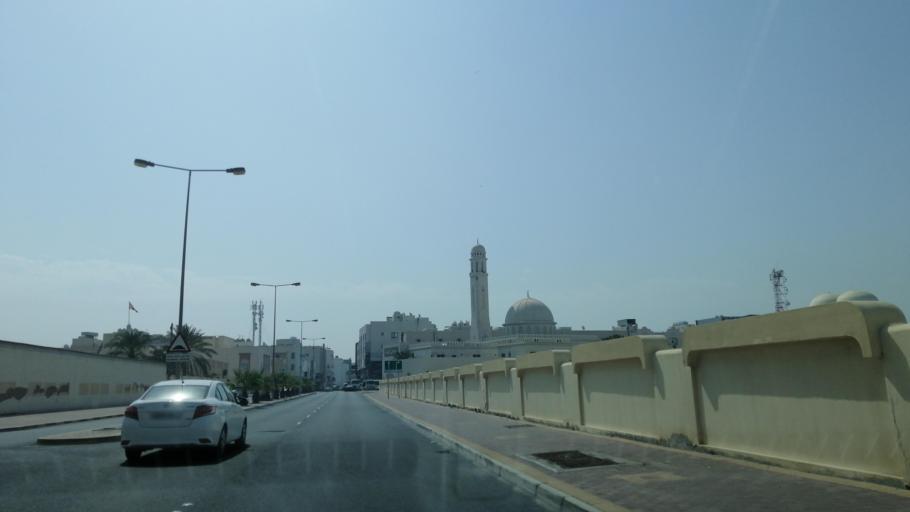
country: BH
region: Muharraq
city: Al Hadd
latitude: 26.2517
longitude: 50.6541
